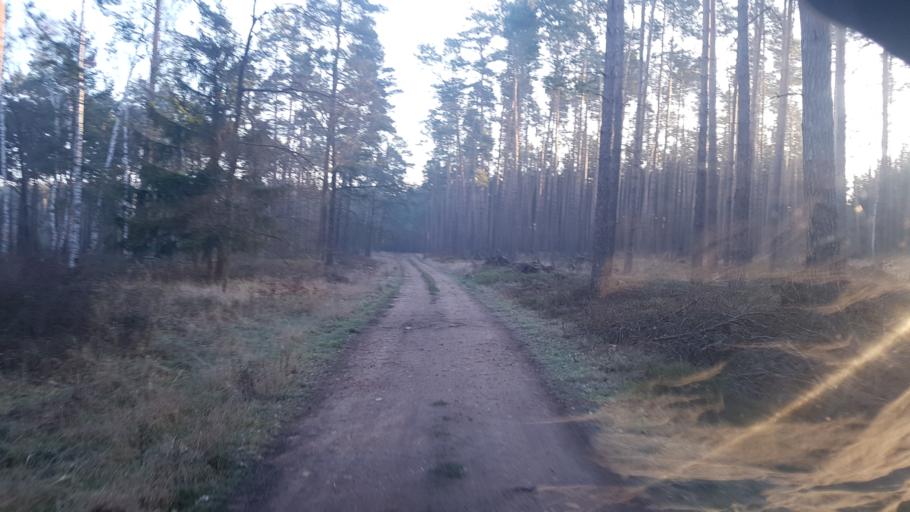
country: DE
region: Brandenburg
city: Crinitz
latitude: 51.6736
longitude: 13.7538
